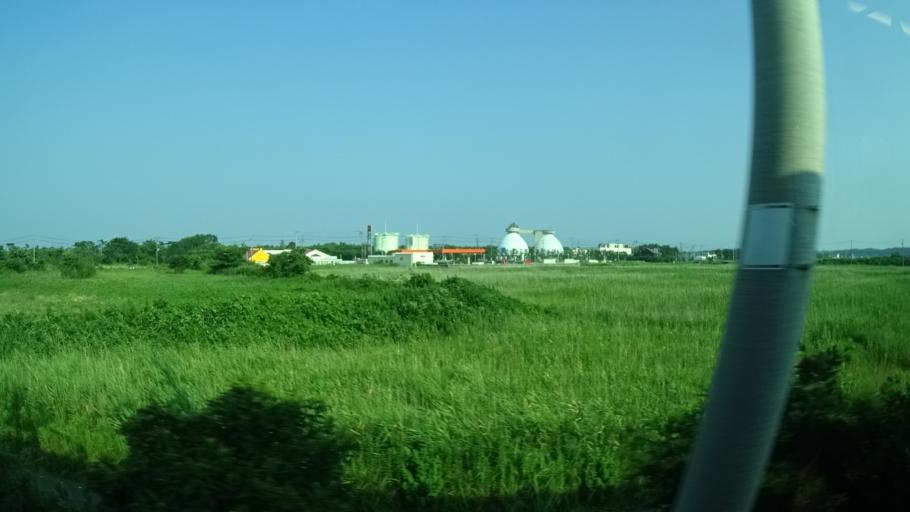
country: JP
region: Ibaraki
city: Takahagi
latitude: 36.6916
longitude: 140.7110
